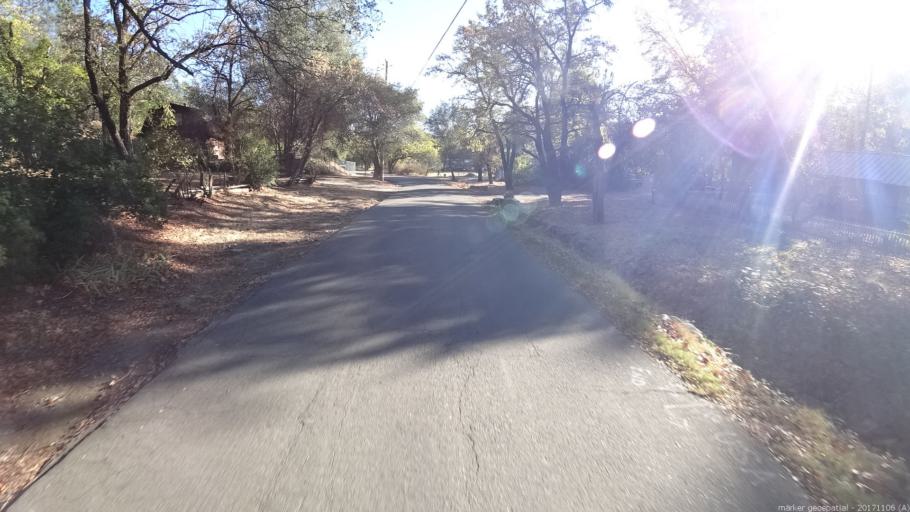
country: US
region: California
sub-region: Shasta County
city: Shasta
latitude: 40.6002
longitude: -122.4903
